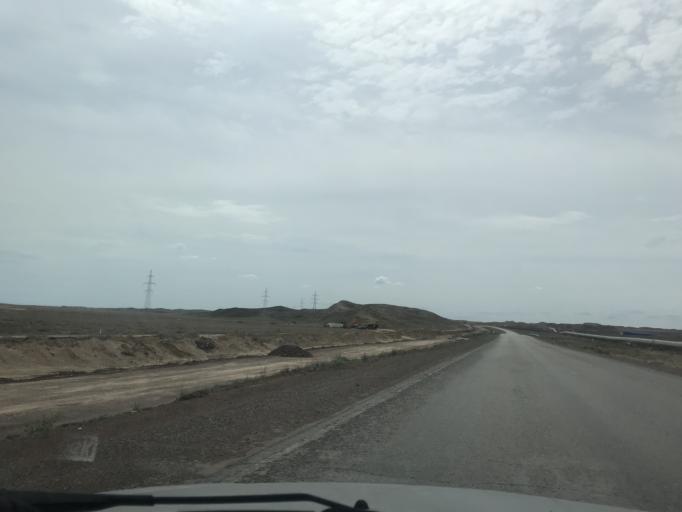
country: KZ
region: Zhambyl
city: Mynaral
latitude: 45.3761
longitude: 73.6551
